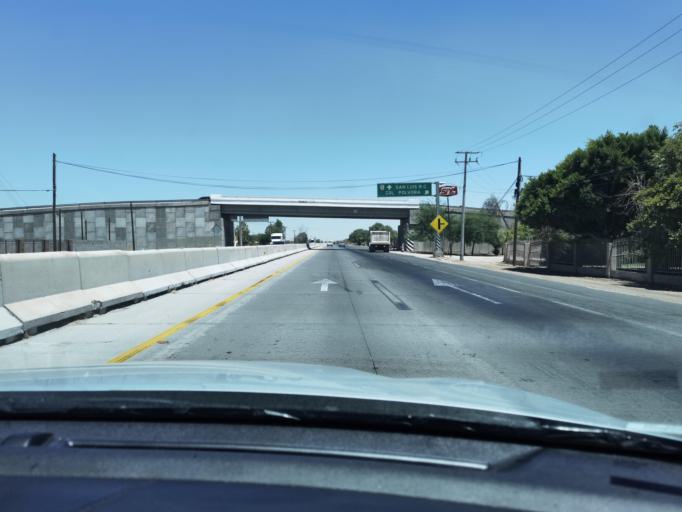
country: MX
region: Baja California
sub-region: Mexicali
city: Ejido Yucatan
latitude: 32.5528
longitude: -115.1957
